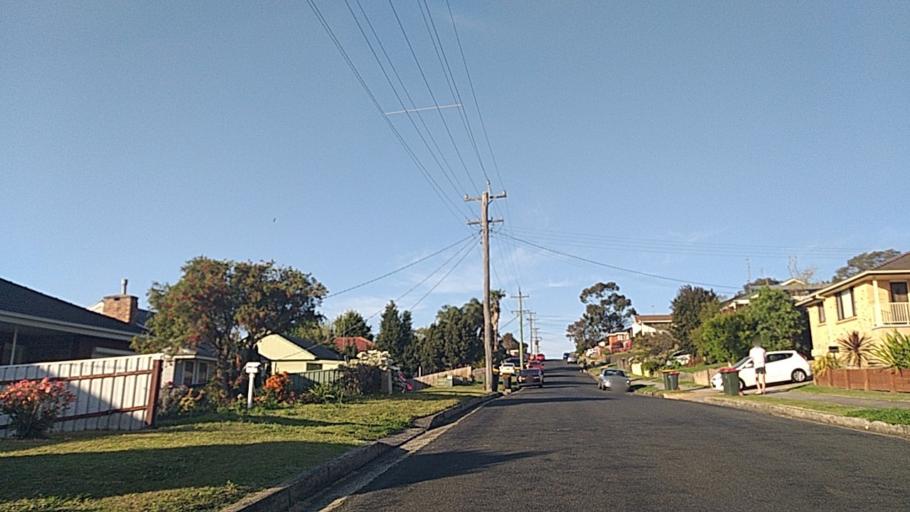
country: AU
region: New South Wales
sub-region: Wollongong
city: Koonawarra
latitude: -34.4862
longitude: 150.8034
